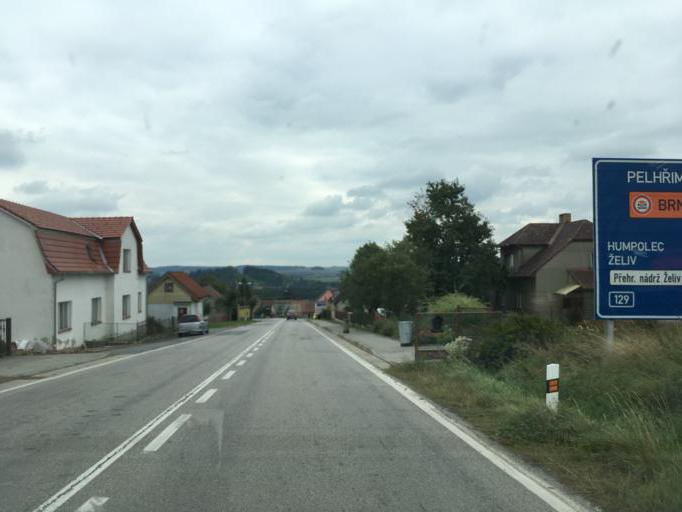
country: CZ
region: Vysocina
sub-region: Okres Pelhrimov
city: Zeliv
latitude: 49.5384
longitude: 15.1659
